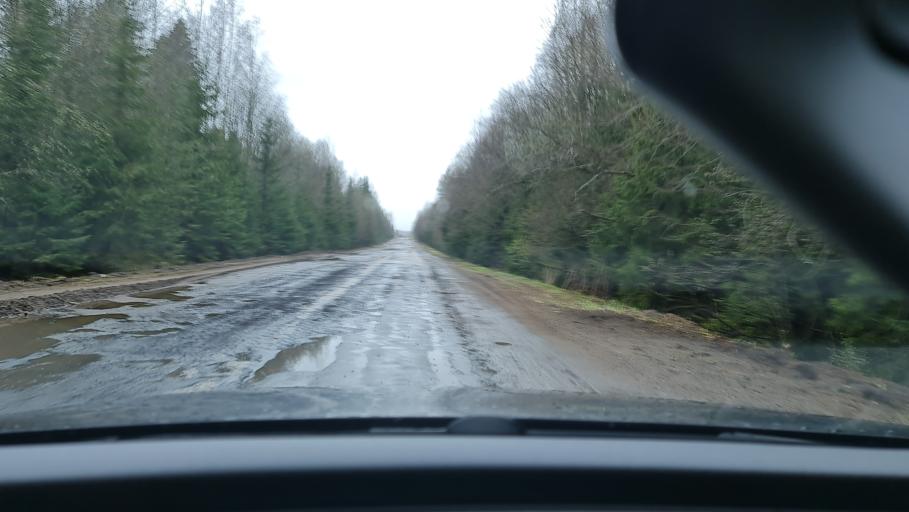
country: RU
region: Novgorod
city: Valday
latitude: 58.0353
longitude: 32.8623
